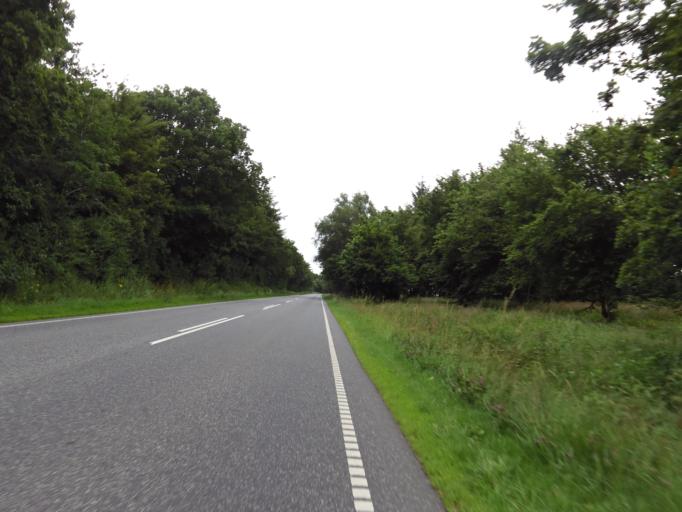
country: DK
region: South Denmark
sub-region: Tonder Kommune
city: Logumkloster
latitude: 55.1568
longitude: 8.9613
